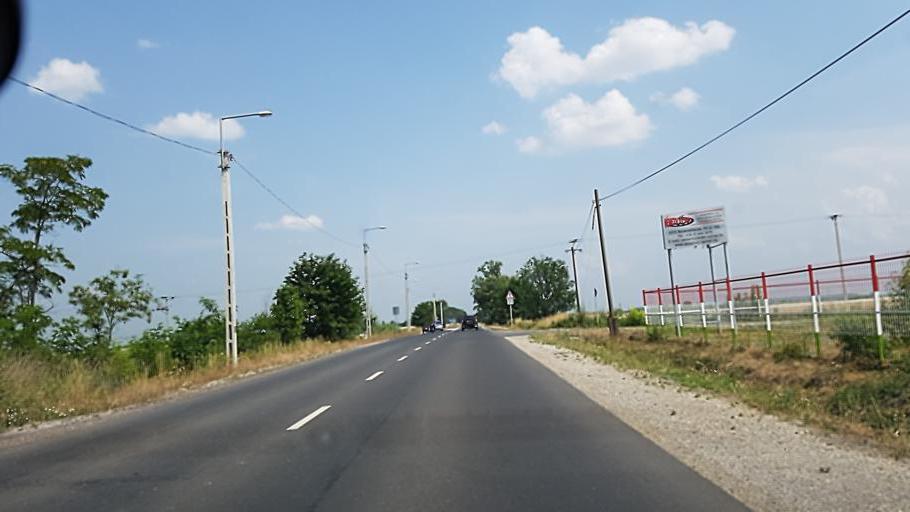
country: HU
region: Heves
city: Besenyotelek
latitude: 47.6926
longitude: 20.4447
